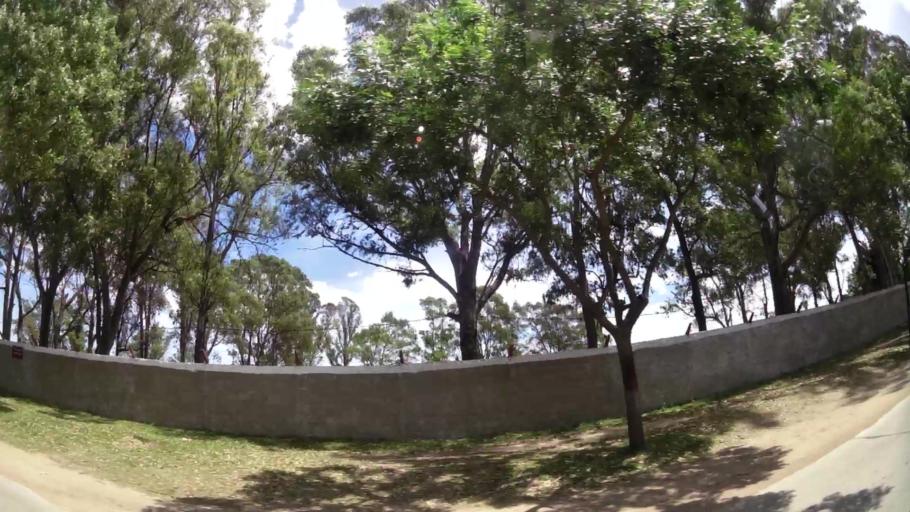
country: UY
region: Montevideo
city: Montevideo
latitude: -34.8621
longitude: -56.2520
